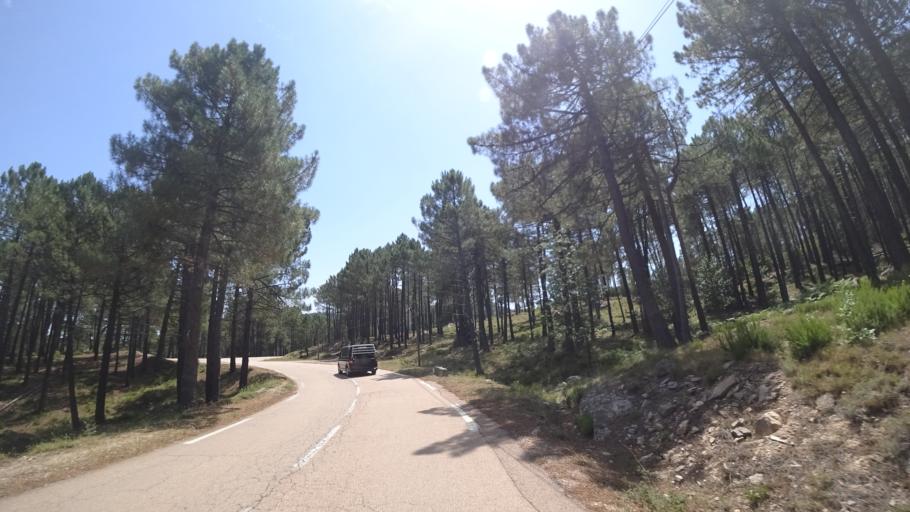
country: FR
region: Corsica
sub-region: Departement de la Corse-du-Sud
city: Zonza
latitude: 41.6731
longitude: 9.2071
